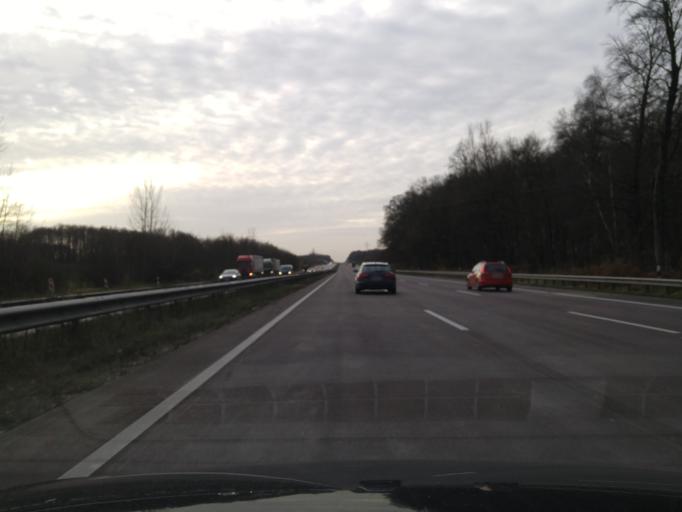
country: DE
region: Schleswig-Holstein
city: Hoisdorf
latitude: 53.6779
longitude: 10.3113
